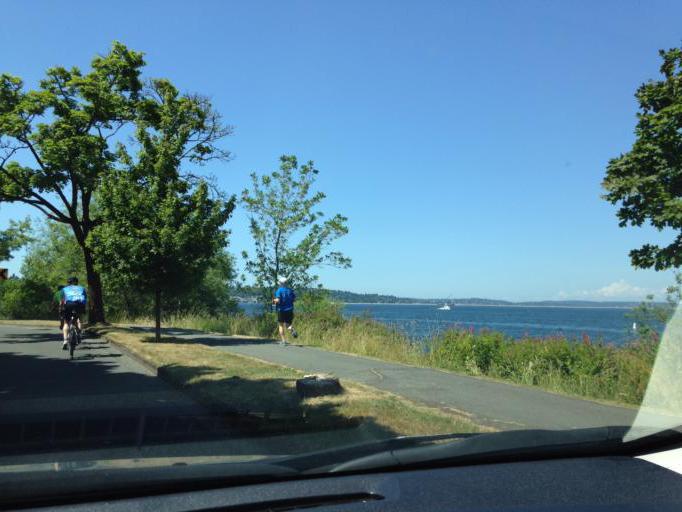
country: US
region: Washington
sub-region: King County
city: Mercer Island
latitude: 47.5675
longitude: -122.2697
